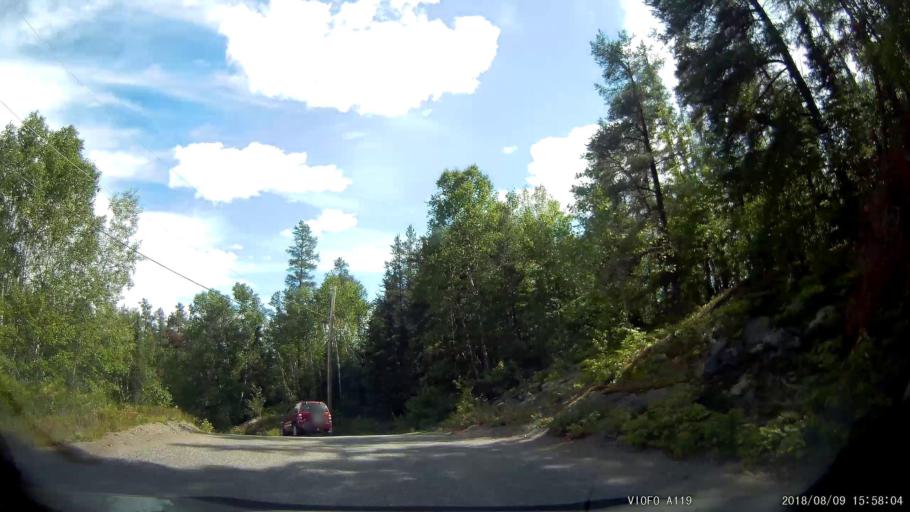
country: CA
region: Ontario
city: Rayside-Balfour
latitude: 46.6064
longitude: -81.5005
